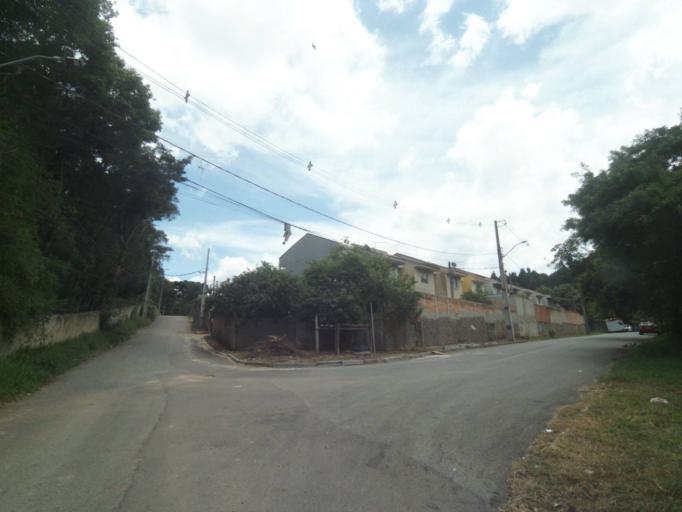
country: BR
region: Parana
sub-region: Curitiba
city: Curitiba
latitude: -25.4678
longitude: -49.3420
